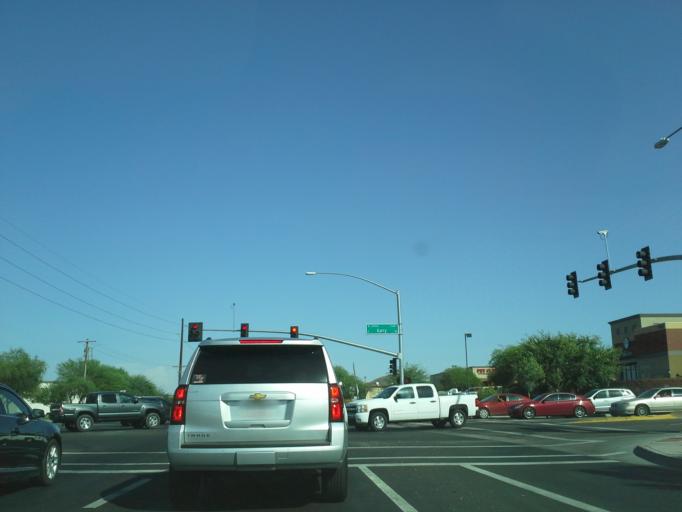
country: US
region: Arizona
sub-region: Pinal County
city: San Tan Valley
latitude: 33.1799
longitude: -111.5852
